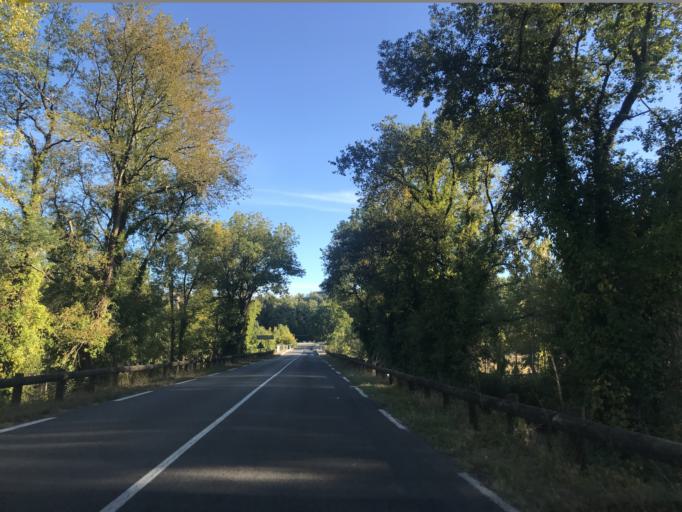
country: FR
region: Aquitaine
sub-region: Departement de la Dordogne
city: La Roche-Chalais
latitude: 45.2095
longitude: 0.0322
